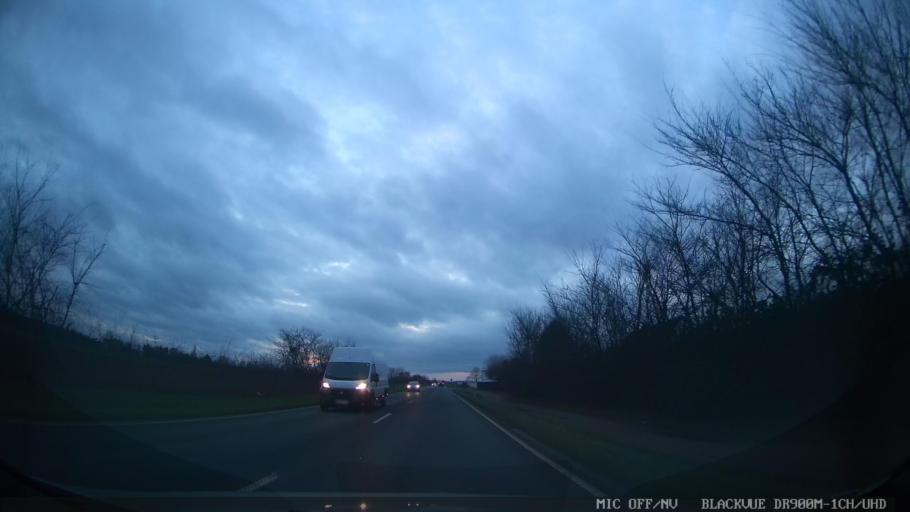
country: DE
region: Hesse
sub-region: Regierungsbezirk Darmstadt
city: Babenhausen
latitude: 49.9518
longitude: 8.9489
